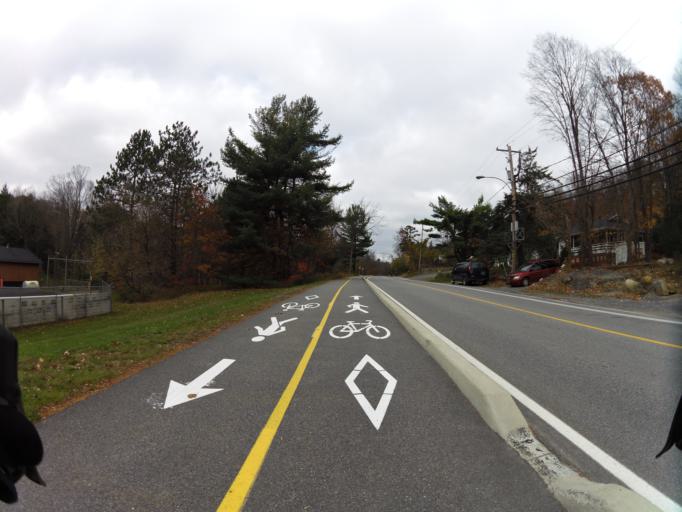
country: CA
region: Quebec
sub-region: Outaouais
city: Gatineau
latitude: 45.5066
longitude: -75.8118
